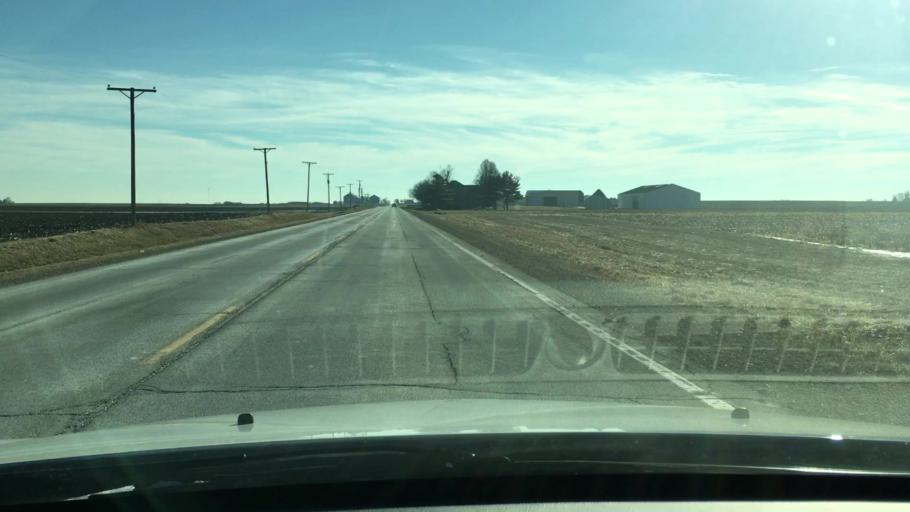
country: US
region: Illinois
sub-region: LaSalle County
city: Mendota
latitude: 41.6115
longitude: -89.1288
